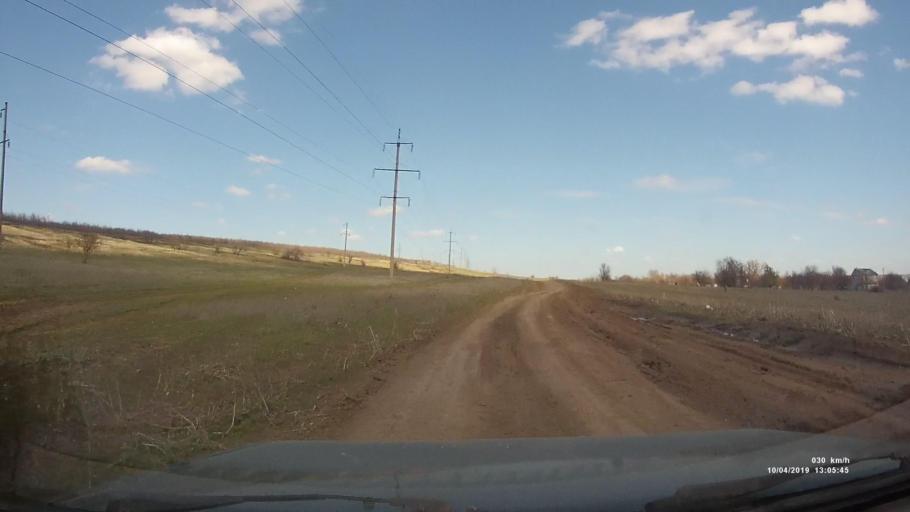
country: RU
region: Rostov
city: Masalovka
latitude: 48.3892
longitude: 40.2334
